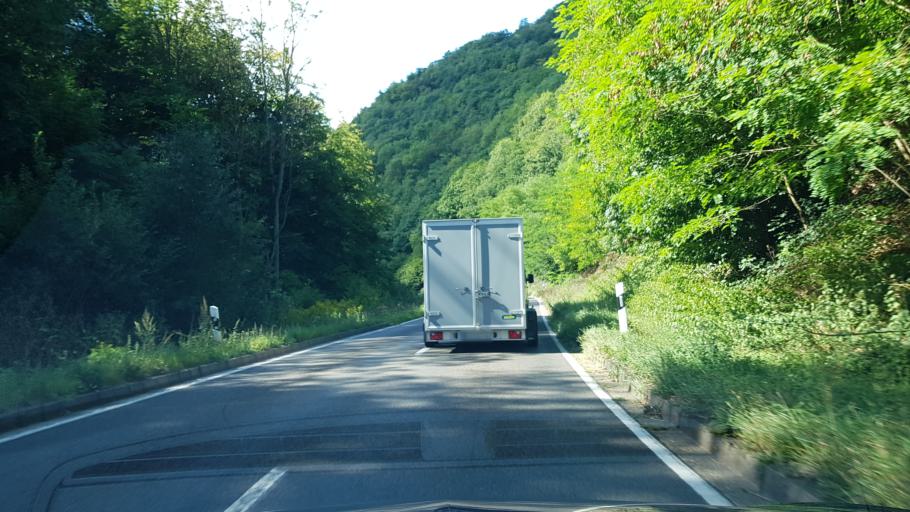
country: DE
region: Rheinland-Pfalz
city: Bruttig-Fankel
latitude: 50.1411
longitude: 7.2494
